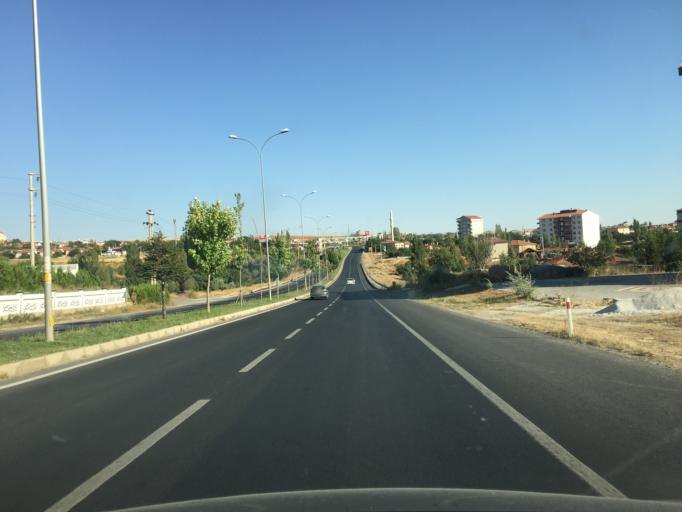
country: TR
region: Kirsehir
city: Kirsehir
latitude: 39.1378
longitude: 34.1824
